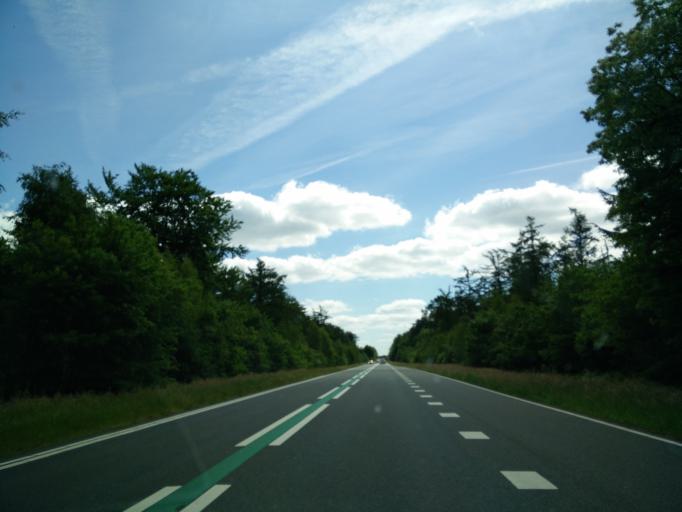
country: NL
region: Drenthe
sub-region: Gemeente Coevorden
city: Sleen
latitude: 52.8132
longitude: 6.6804
